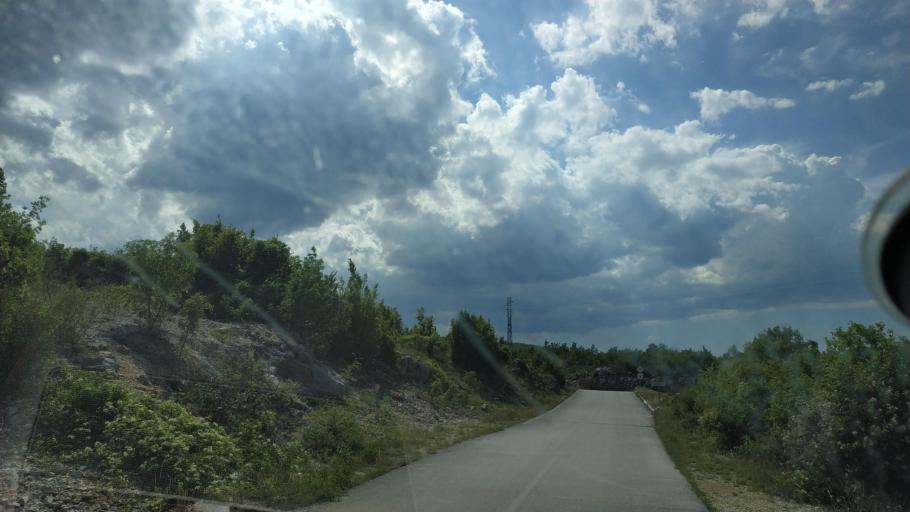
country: HR
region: Splitsko-Dalmatinska
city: Dugopolje
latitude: 43.5811
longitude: 16.6527
